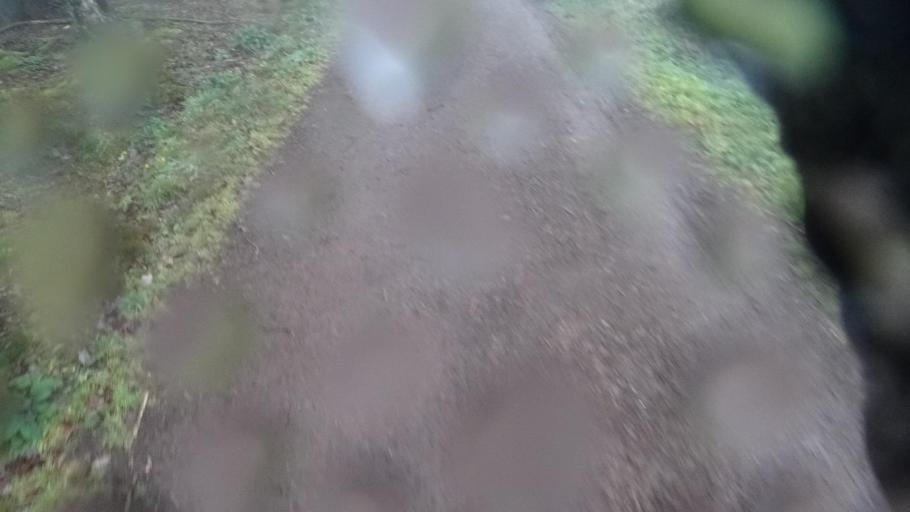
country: DE
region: Rheinland-Pfalz
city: Karbach
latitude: 50.1770
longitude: 7.6064
